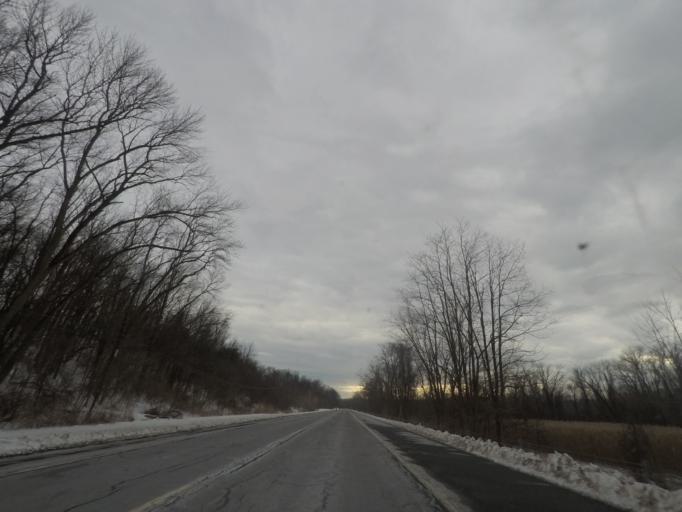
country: US
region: New York
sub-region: Rensselaer County
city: Castleton-on-Hudson
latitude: 42.5647
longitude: -73.7422
